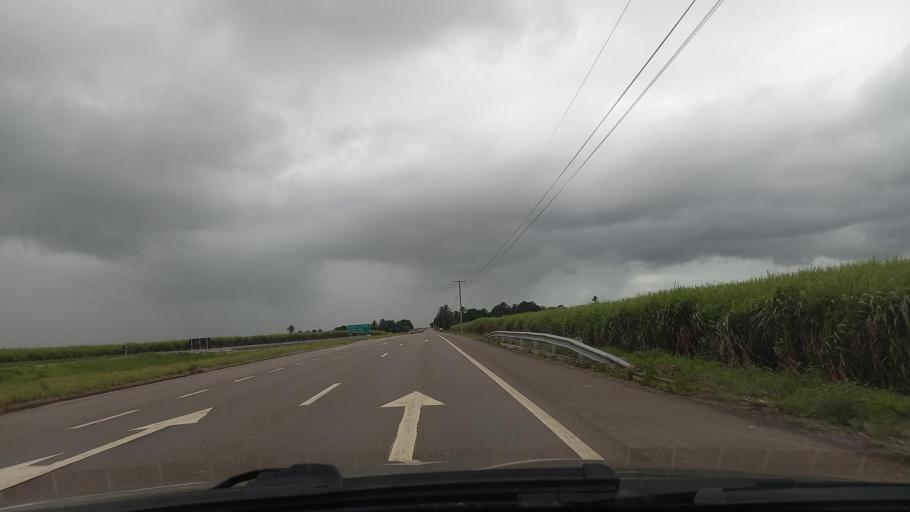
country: BR
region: Alagoas
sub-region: Limoeiro De Anadia
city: Cajueiro
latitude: -9.7622
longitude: -36.4338
